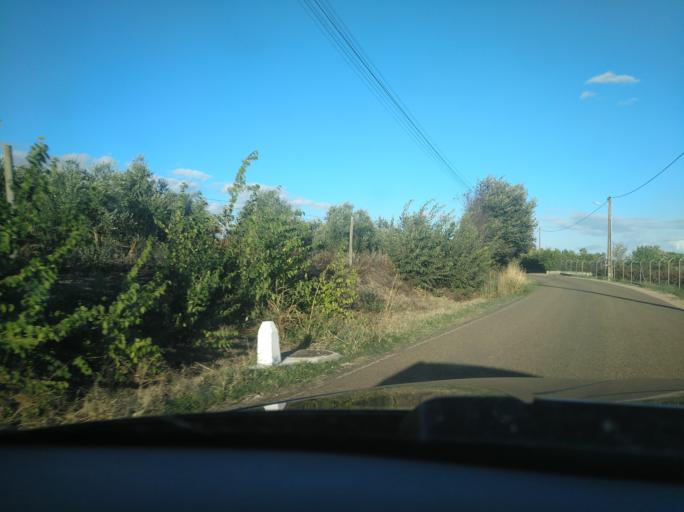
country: PT
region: Portalegre
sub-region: Campo Maior
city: Campo Maior
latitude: 39.0213
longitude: -7.0535
